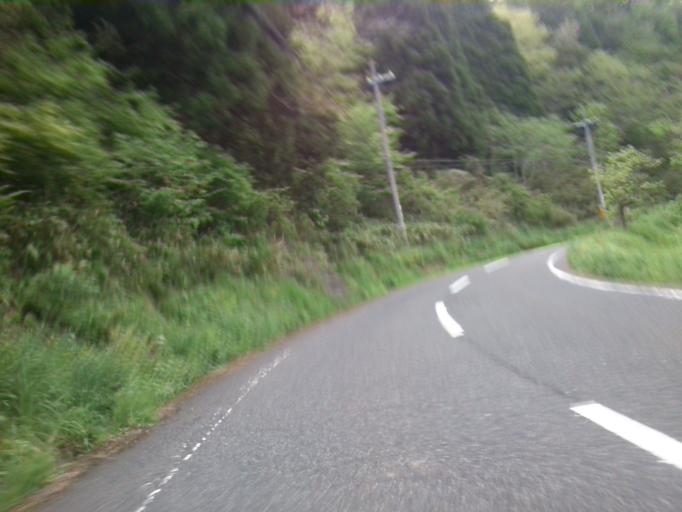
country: JP
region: Kyoto
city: Miyazu
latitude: 35.6870
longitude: 135.1572
